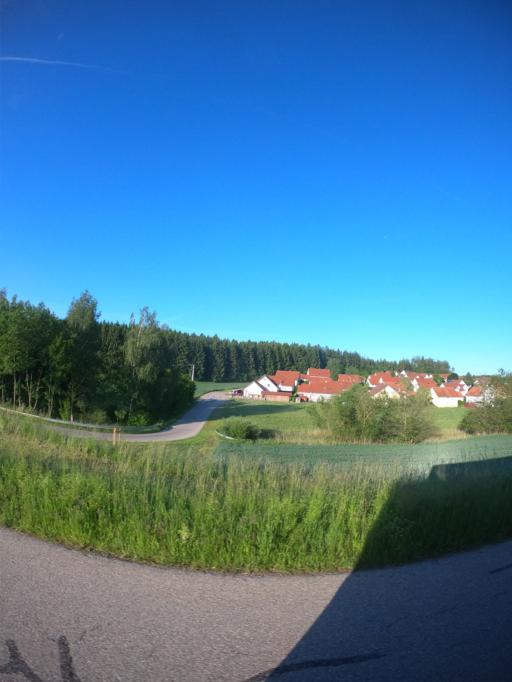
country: DE
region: Bavaria
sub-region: Upper Bavaria
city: Inning am Holz
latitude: 48.3456
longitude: 12.0822
